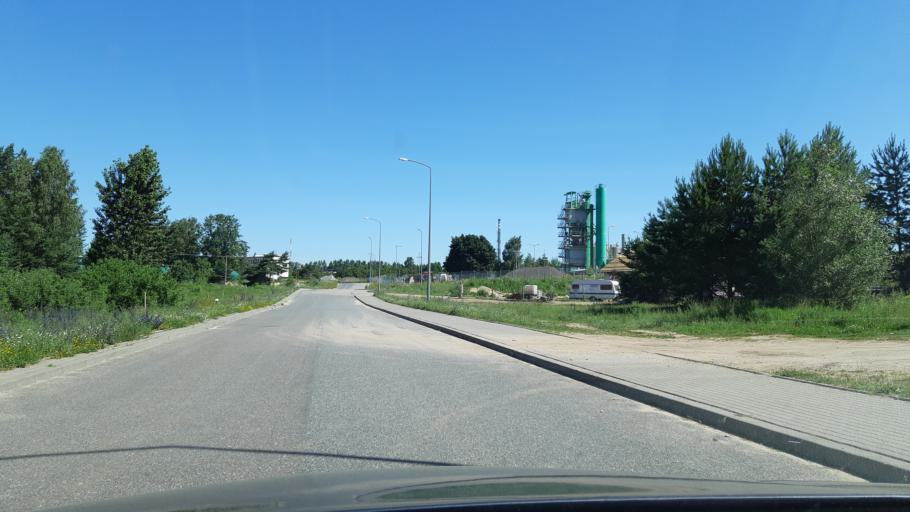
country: PL
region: Warmian-Masurian Voivodeship
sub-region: Powiat mragowski
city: Mragowo
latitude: 53.8481
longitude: 21.2956
